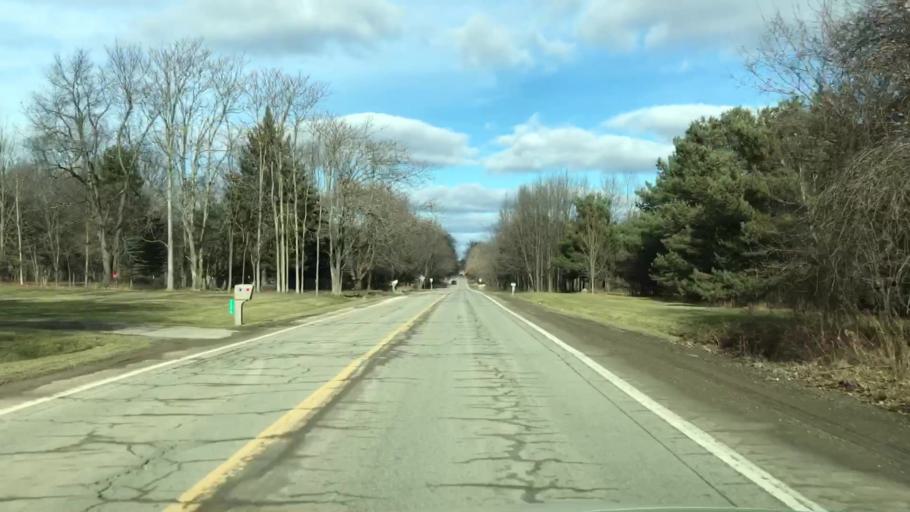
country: US
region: Michigan
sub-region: Oakland County
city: Lake Orion
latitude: 42.7609
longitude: -83.1977
